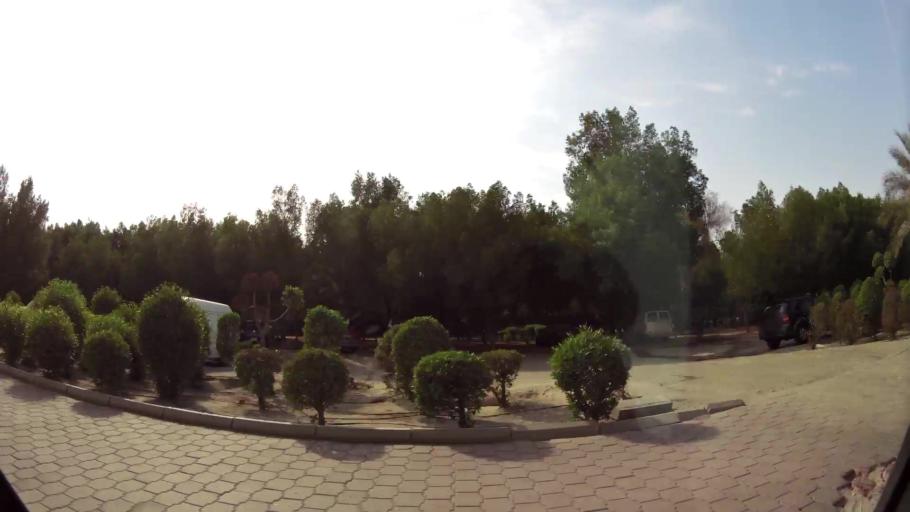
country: KW
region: Al Farwaniyah
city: Al Farwaniyah
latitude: 29.2913
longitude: 47.9665
